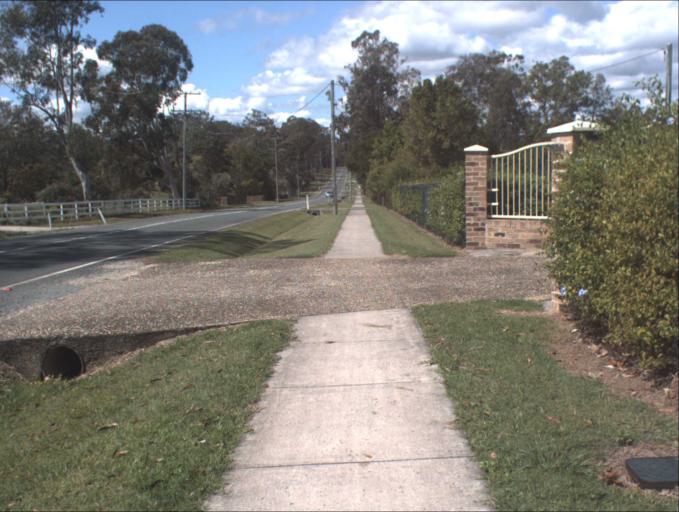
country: AU
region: Queensland
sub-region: Logan
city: Park Ridge South
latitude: -27.7271
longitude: 153.0394
